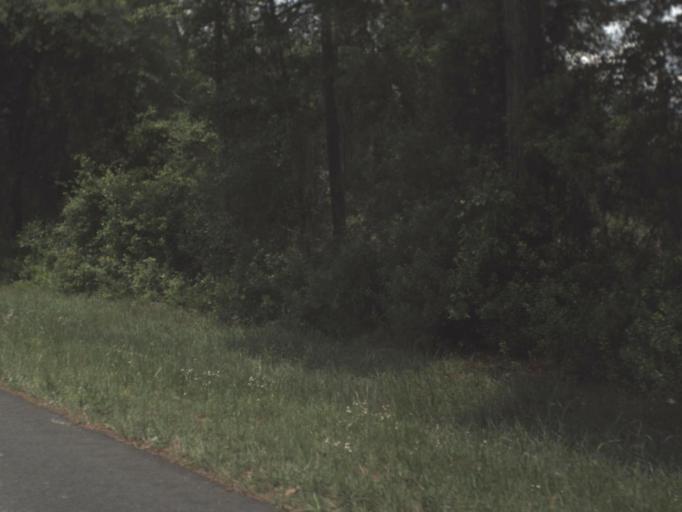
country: US
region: Florida
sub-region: Columbia County
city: Five Points
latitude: 30.4849
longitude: -82.6602
